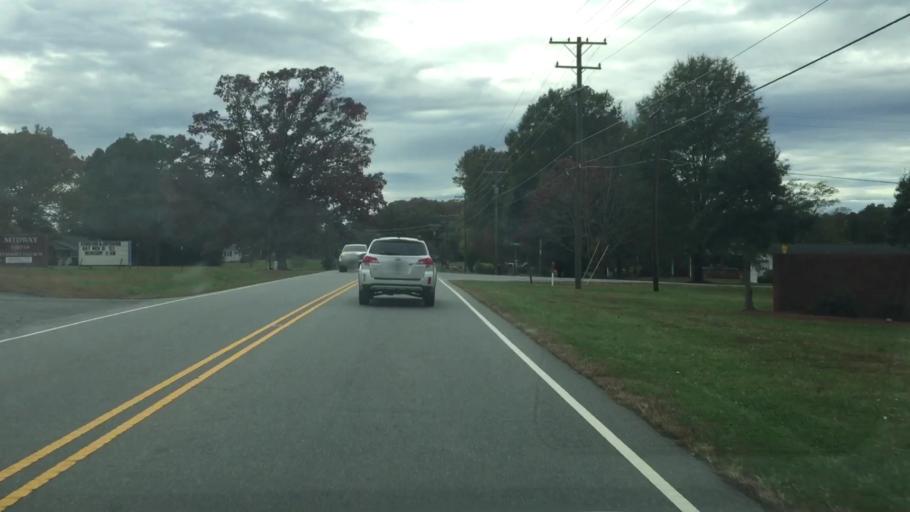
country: US
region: North Carolina
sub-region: Rockingham County
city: Wentworth
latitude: 36.2746
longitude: -79.7817
